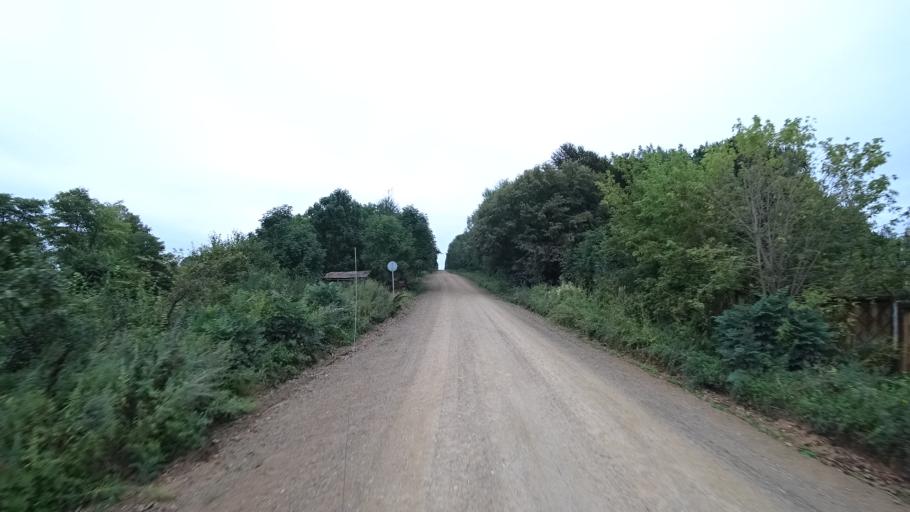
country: RU
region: Primorskiy
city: Rettikhovka
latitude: 44.1719
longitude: 132.8800
